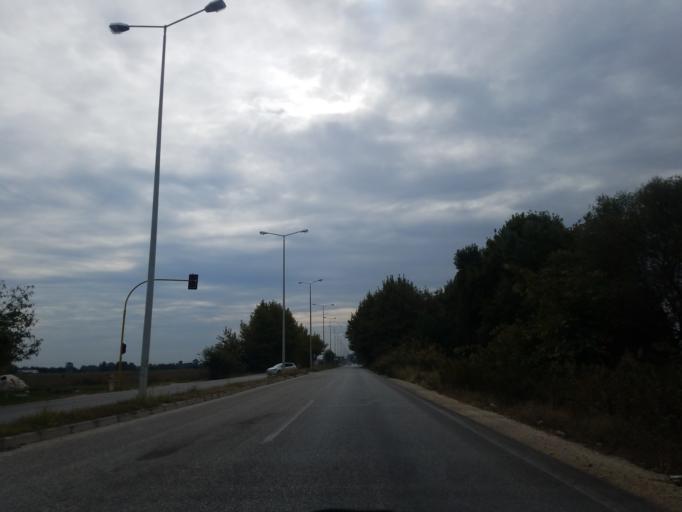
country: GR
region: Thessaly
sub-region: Trikala
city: Pyrgetos
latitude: 39.5284
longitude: 21.7458
